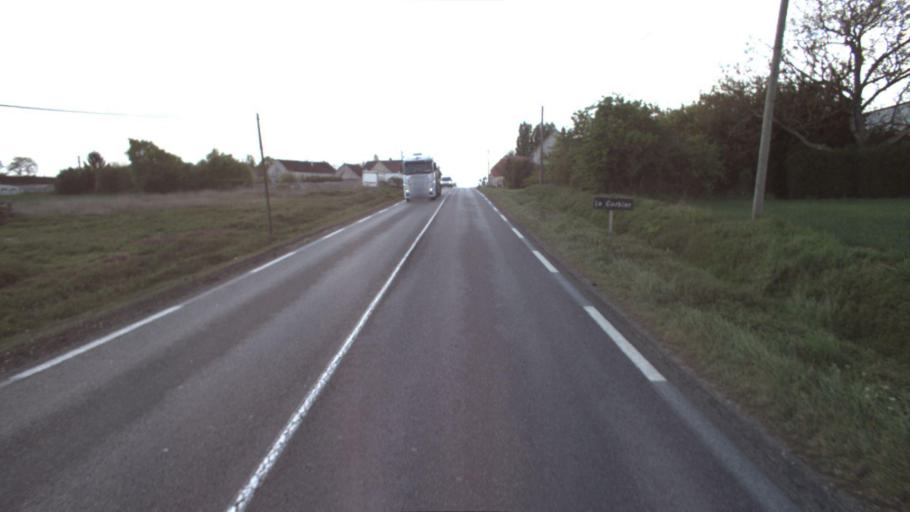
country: FR
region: Ile-de-France
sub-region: Departement de Seine-et-Marne
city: Jouy-le-Chatel
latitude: 48.6885
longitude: 3.1273
